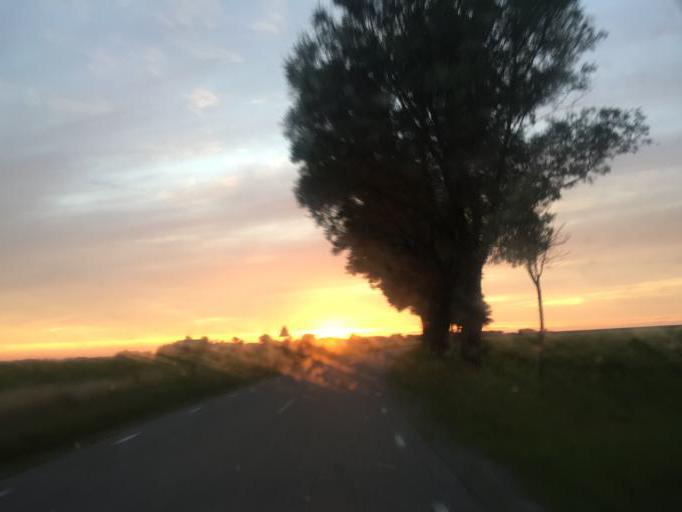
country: NL
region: Friesland
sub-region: Gemeente Dongeradeel
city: Anjum
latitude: 53.3904
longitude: 6.1026
